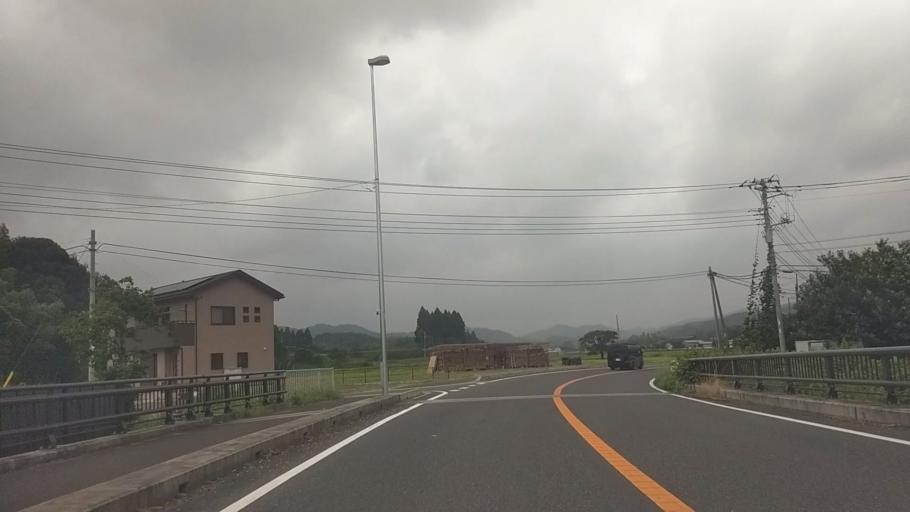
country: JP
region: Chiba
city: Kawaguchi
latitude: 35.1355
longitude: 139.9993
